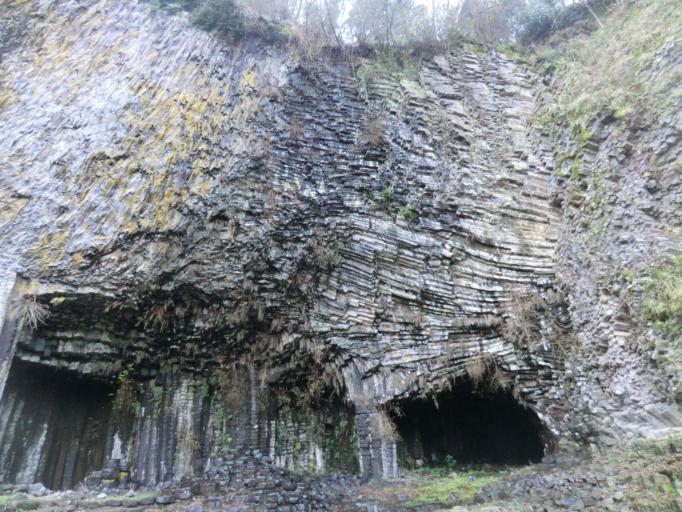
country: JP
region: Hyogo
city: Toyooka
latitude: 35.5883
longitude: 134.8047
